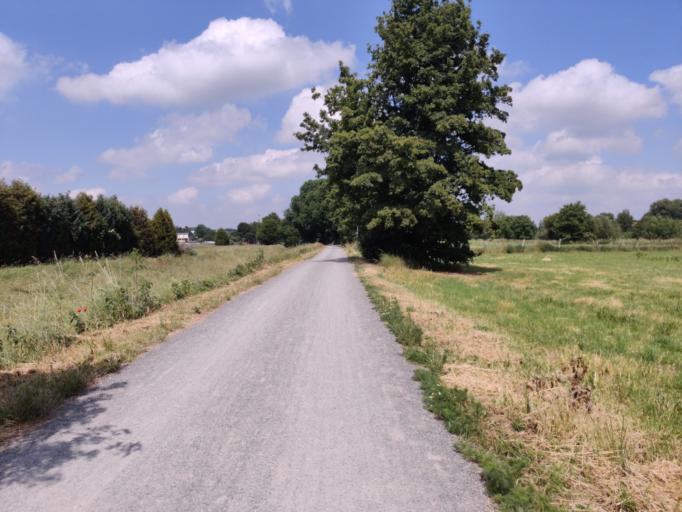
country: DE
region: Lower Saxony
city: Hildesheim
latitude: 52.1587
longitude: 9.9262
